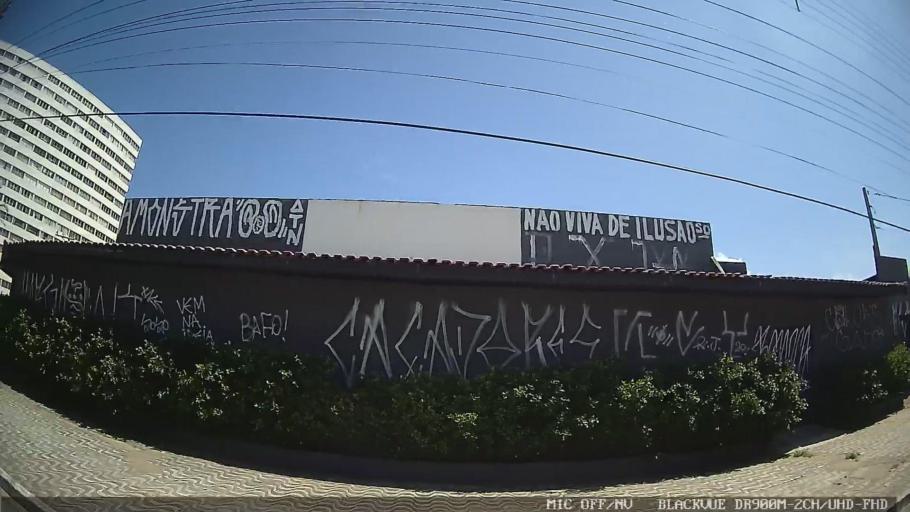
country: BR
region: Sao Paulo
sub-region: Peruibe
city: Peruibe
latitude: -24.3244
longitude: -46.9951
